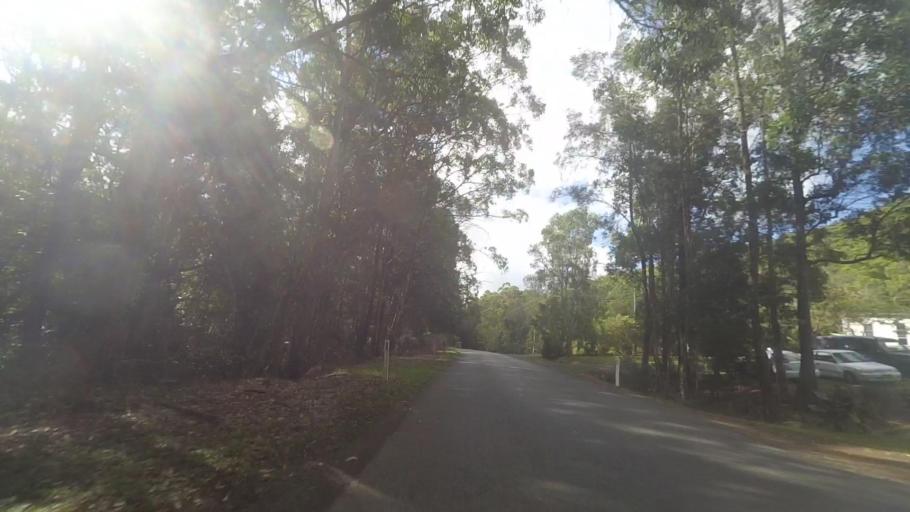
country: AU
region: New South Wales
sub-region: Great Lakes
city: Forster
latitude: -32.3954
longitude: 152.4568
